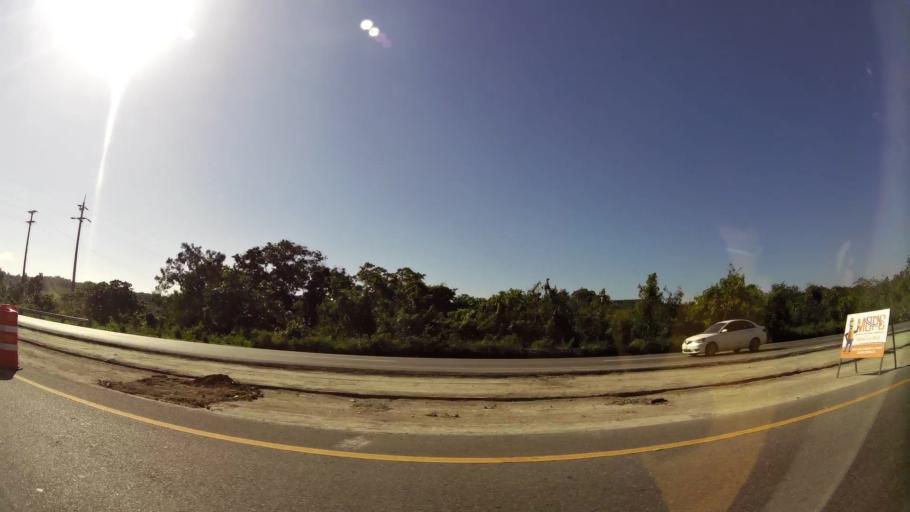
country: DO
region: San Cristobal
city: El Carril
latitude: 18.4389
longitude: -70.0096
